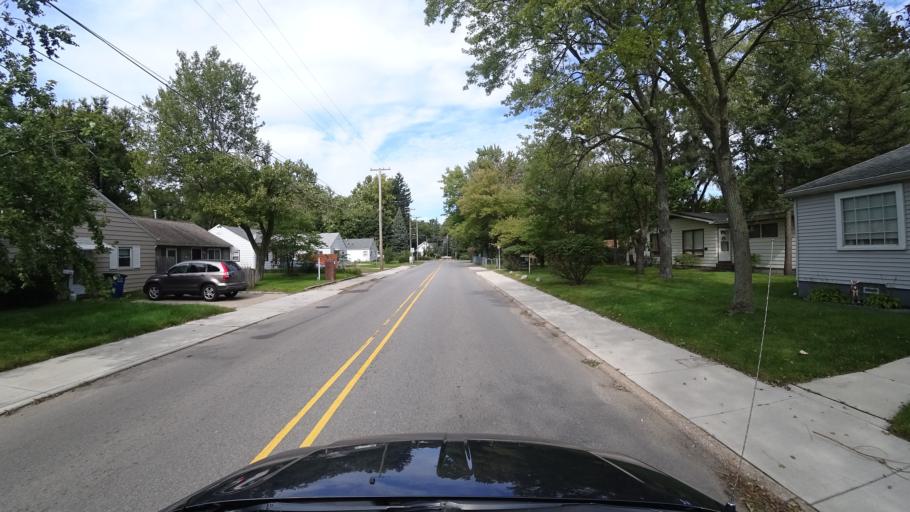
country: US
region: Indiana
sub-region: LaPorte County
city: Trail Creek
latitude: 41.7160
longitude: -86.8698
